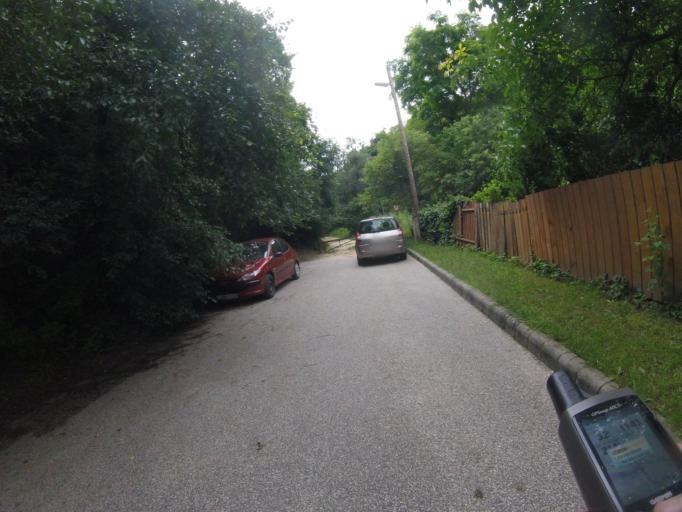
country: HU
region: Pest
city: Toeroekbalint
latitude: 47.4252
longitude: 18.9124
